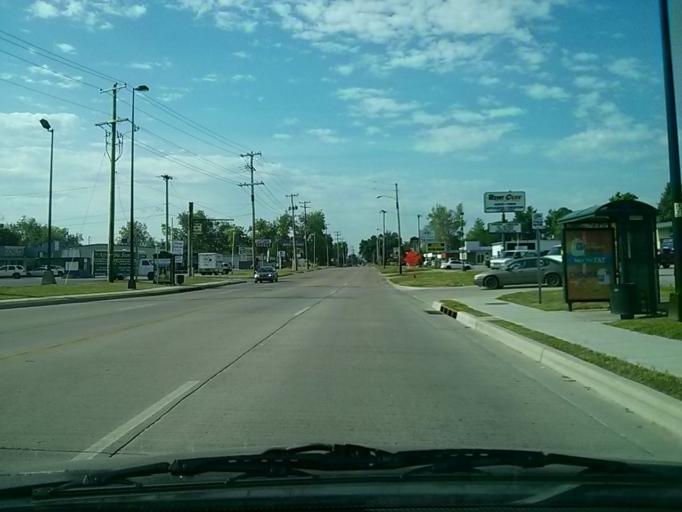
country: US
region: Oklahoma
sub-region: Tulsa County
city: Jenks
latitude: 36.0880
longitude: -95.9758
